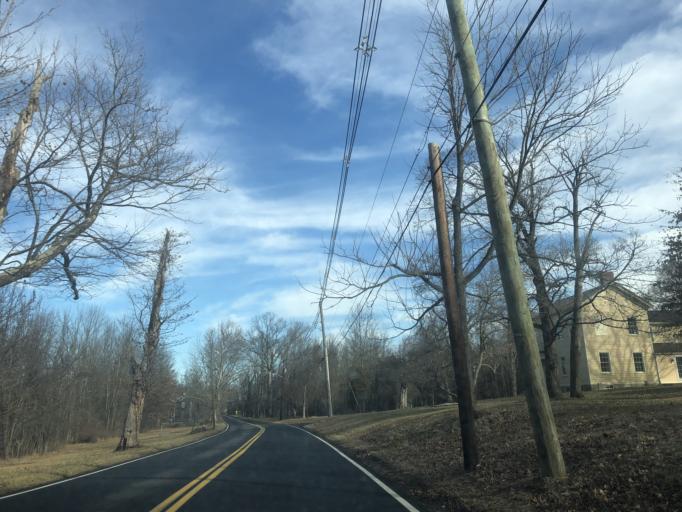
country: US
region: New Jersey
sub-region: Somerset County
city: Kingston
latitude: 40.3656
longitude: -74.6175
